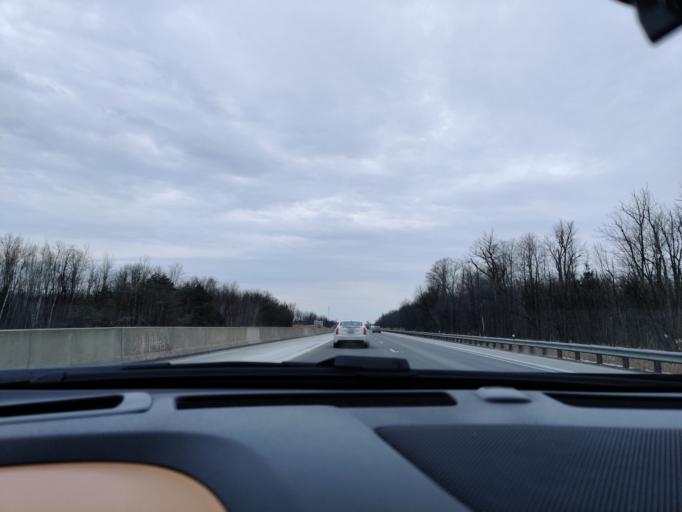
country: CA
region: Ontario
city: Prescott
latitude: 44.7314
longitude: -75.5129
